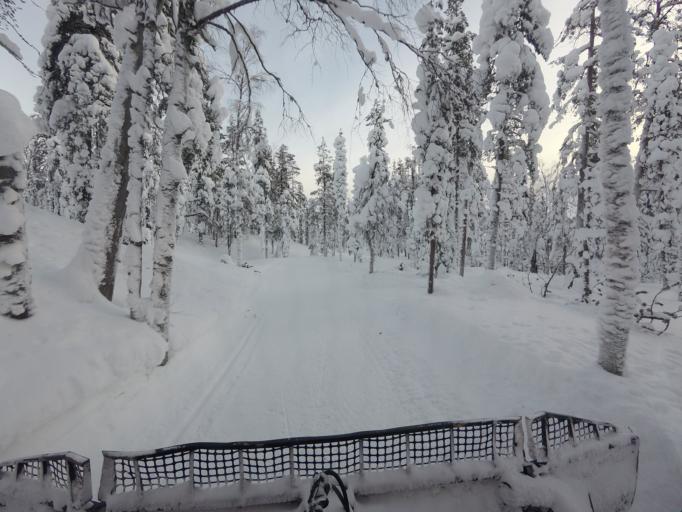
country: FI
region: Lapland
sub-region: Tunturi-Lappi
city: Kolari
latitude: 67.6495
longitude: 24.2403
